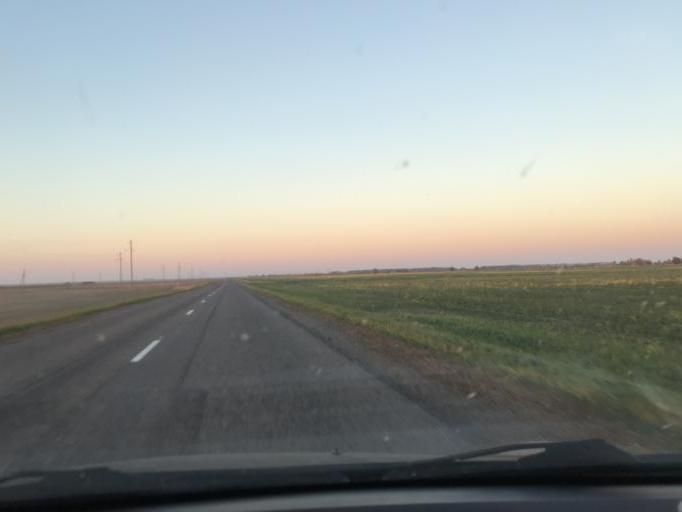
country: BY
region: Gomel
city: Loyew
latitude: 52.1244
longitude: 30.5830
